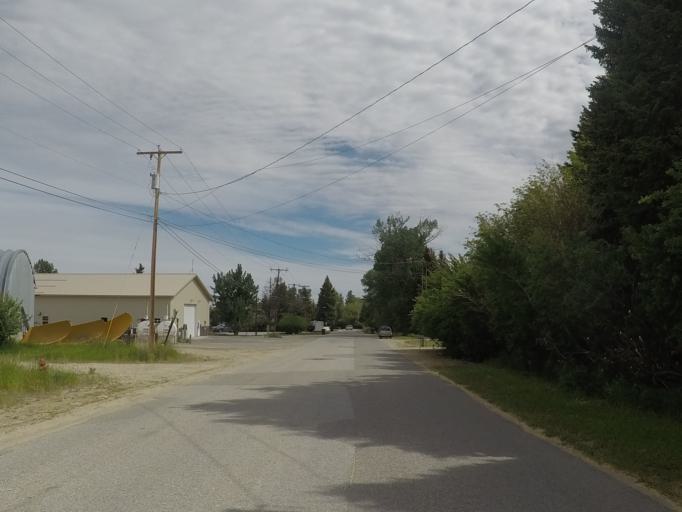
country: US
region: Montana
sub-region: Carbon County
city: Red Lodge
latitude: 45.1729
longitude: -109.2555
